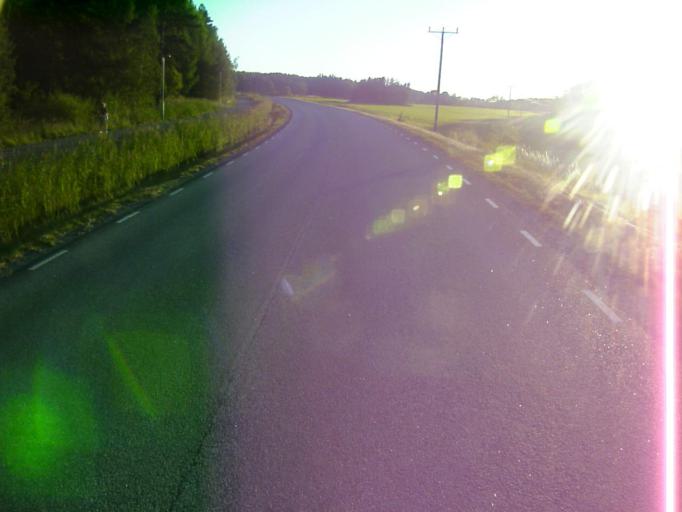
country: SE
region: Soedermanland
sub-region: Eskilstuna Kommun
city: Torshalla
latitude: 59.4167
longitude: 16.4497
